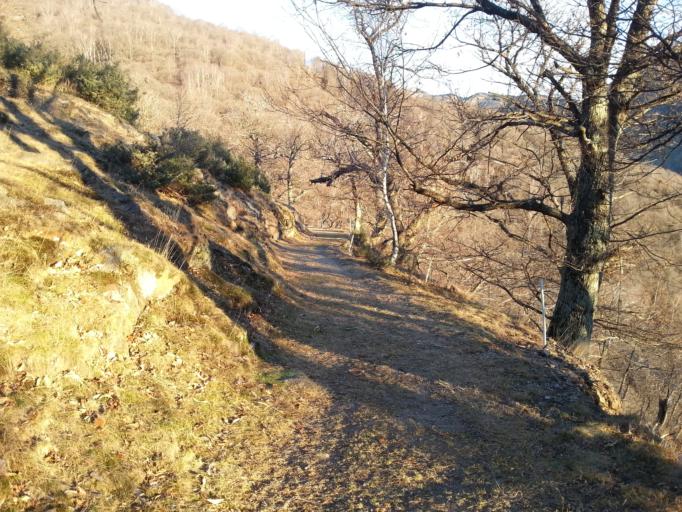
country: CH
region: Ticino
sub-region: Lugano District
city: Gravesano
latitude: 46.0443
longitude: 8.8792
